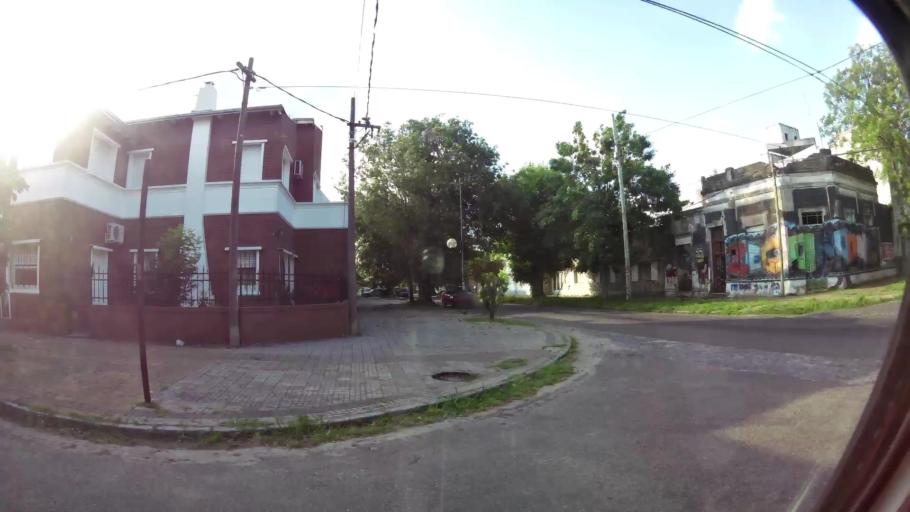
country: AR
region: Buenos Aires
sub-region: Partido de La Plata
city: La Plata
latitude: -34.8958
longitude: -57.9595
